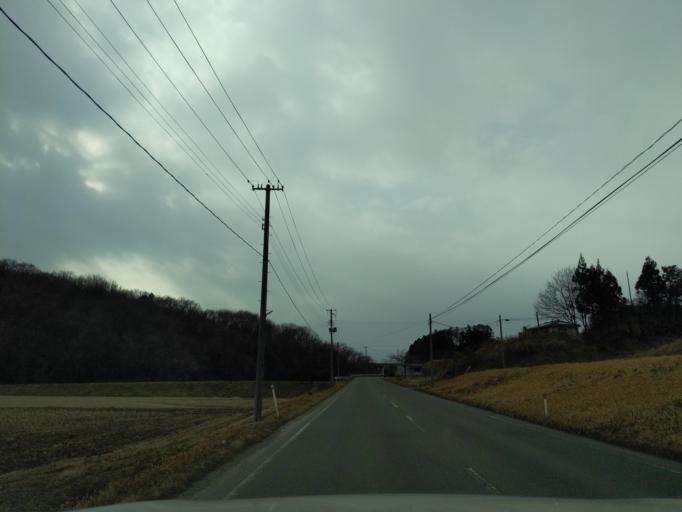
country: JP
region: Fukushima
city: Koriyama
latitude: 37.4522
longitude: 140.4183
